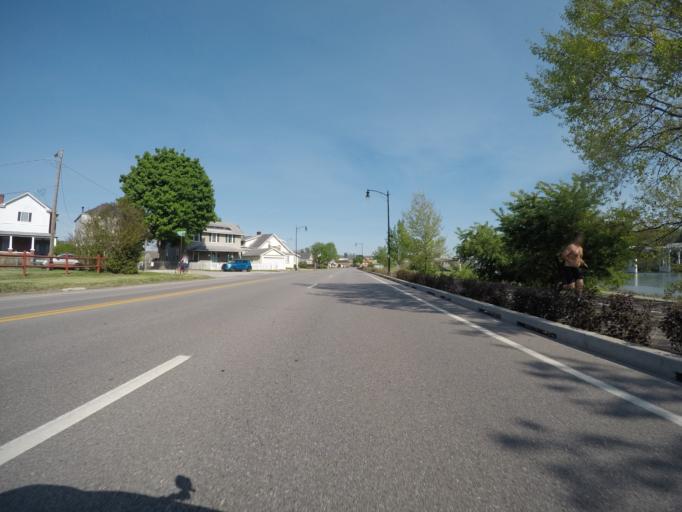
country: US
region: West Virginia
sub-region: Kanawha County
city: Charleston
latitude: 38.3586
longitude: -81.6505
